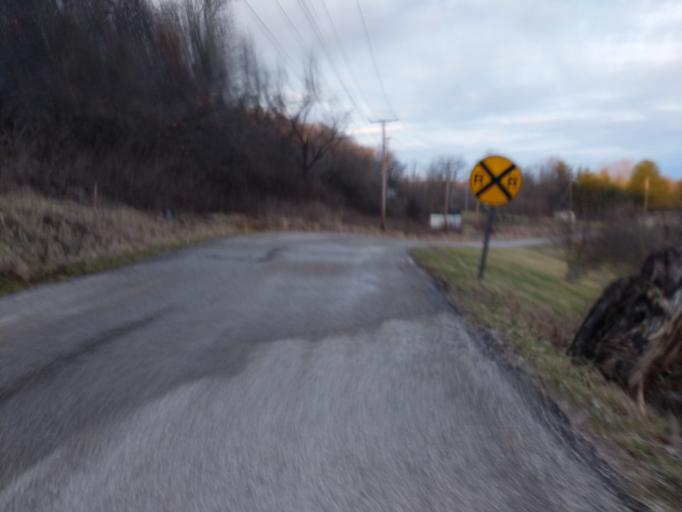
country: US
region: Ohio
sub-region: Athens County
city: Athens
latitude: 39.3339
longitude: -82.1289
